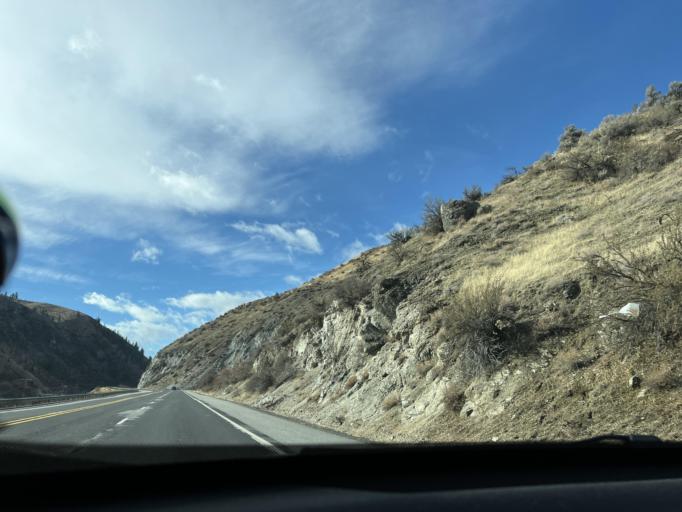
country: US
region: Washington
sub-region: Chelan County
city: Manson
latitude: 47.8351
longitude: -120.1099
